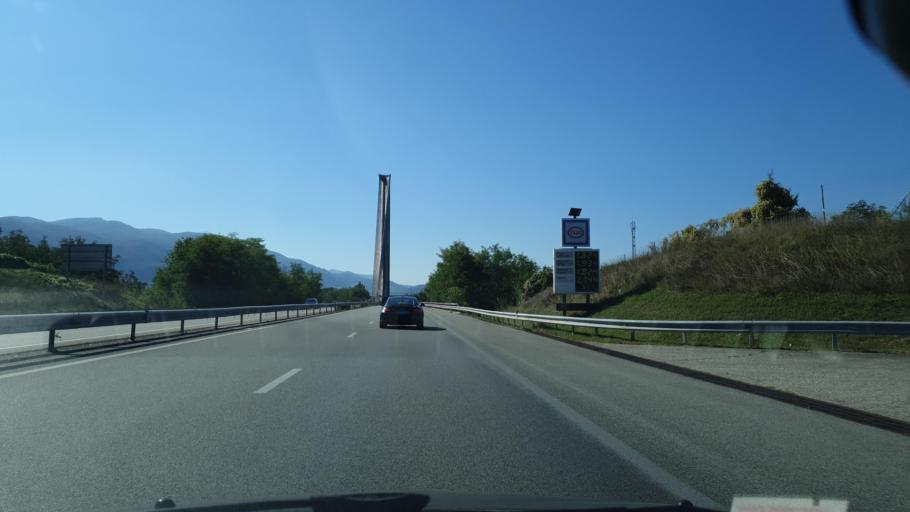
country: FR
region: Rhone-Alpes
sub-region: Departement de l'Isere
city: Saint-Lattier
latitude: 45.0854
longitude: 5.2161
